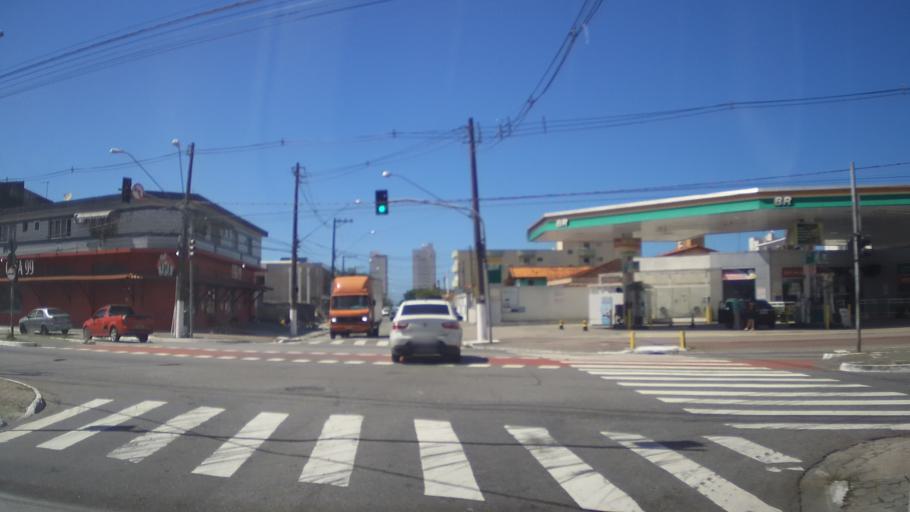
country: BR
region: Sao Paulo
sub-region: Mongagua
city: Mongagua
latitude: -24.0409
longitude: -46.5169
